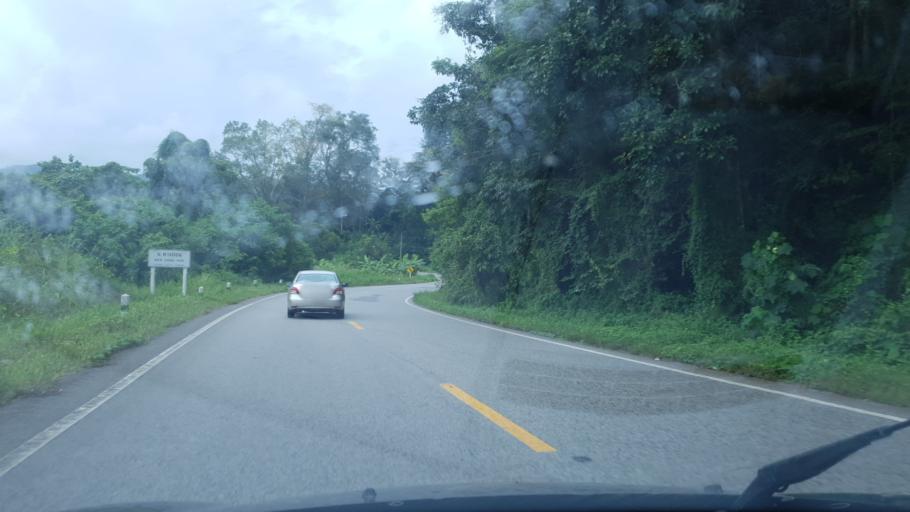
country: TH
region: Mae Hong Son
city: Khun Yuam
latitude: 18.7042
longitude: 97.9140
